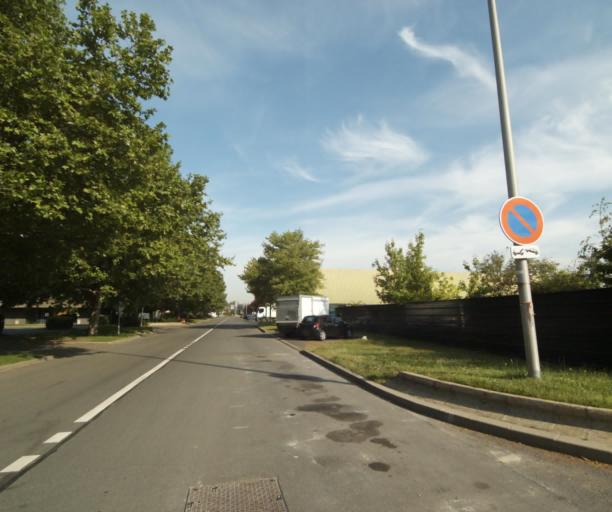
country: FR
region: Ile-de-France
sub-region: Departement des Hauts-de-Seine
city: Bois-Colombes
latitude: 48.9420
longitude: 2.2762
